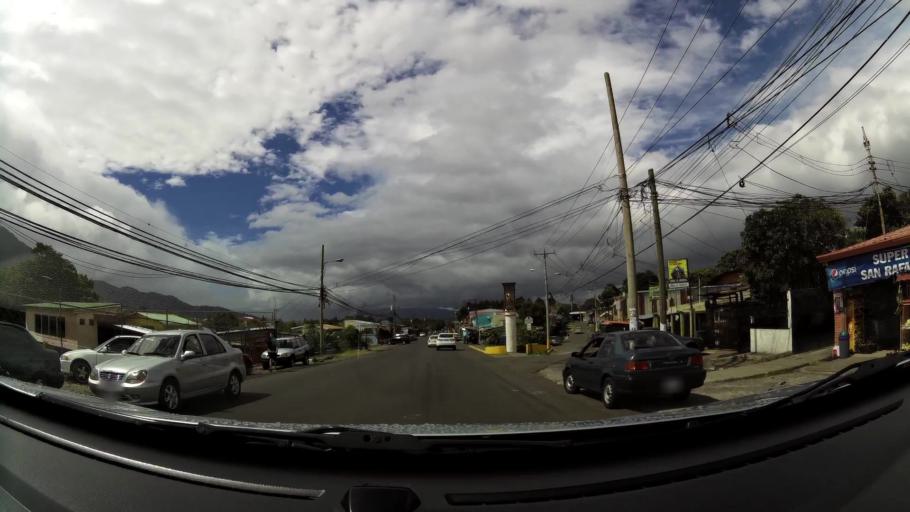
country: CR
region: Cartago
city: Tres Rios
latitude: 9.9081
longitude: -83.9772
